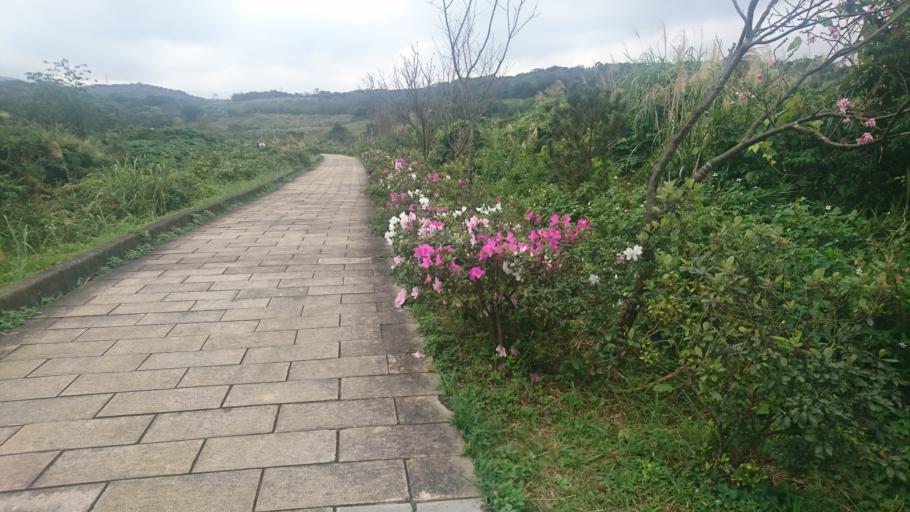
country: TW
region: Taipei
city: Taipei
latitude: 25.2639
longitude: 121.5160
